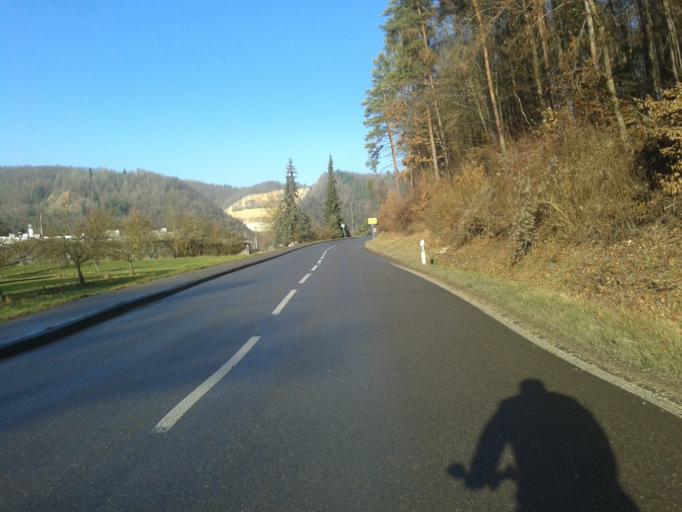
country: DE
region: Baden-Wuerttemberg
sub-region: Tuebingen Region
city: Erbach
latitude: 48.4085
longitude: 9.8713
